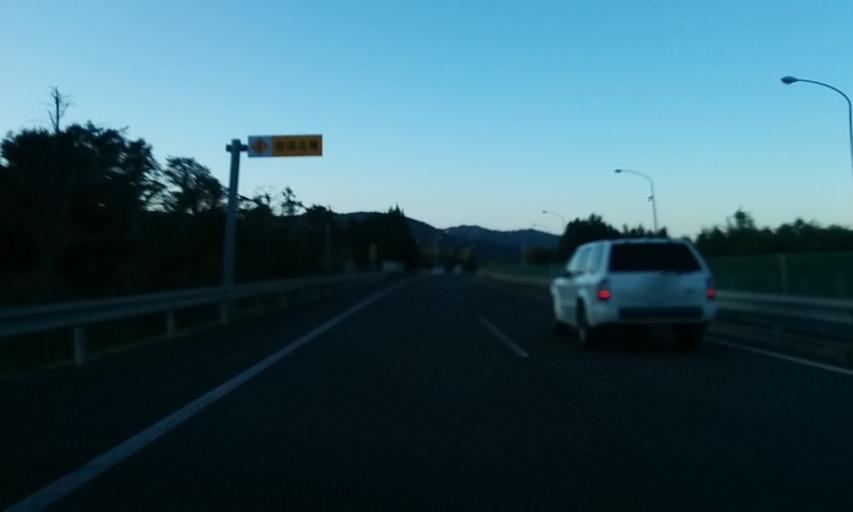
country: JP
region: Kyoto
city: Fukuchiyama
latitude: 35.1633
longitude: 135.1190
